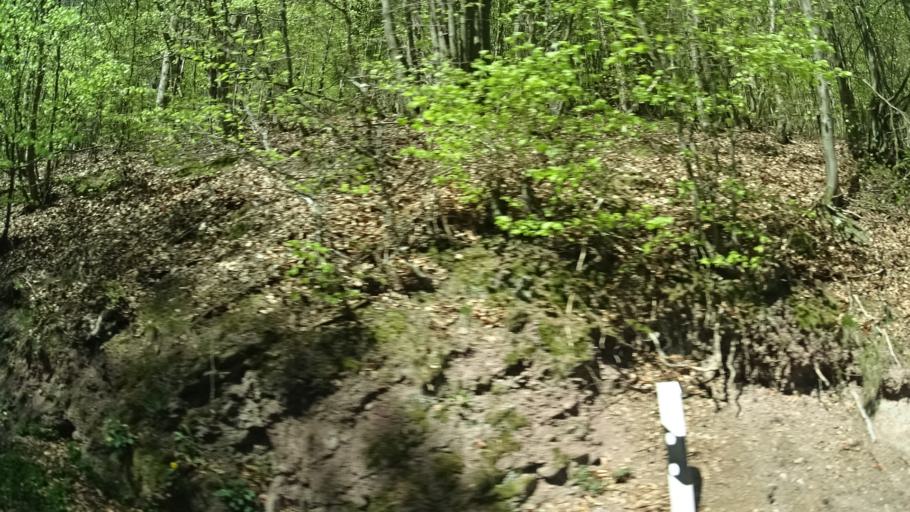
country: DE
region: Thuringia
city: Sankt Kilian
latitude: 50.5111
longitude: 10.8330
